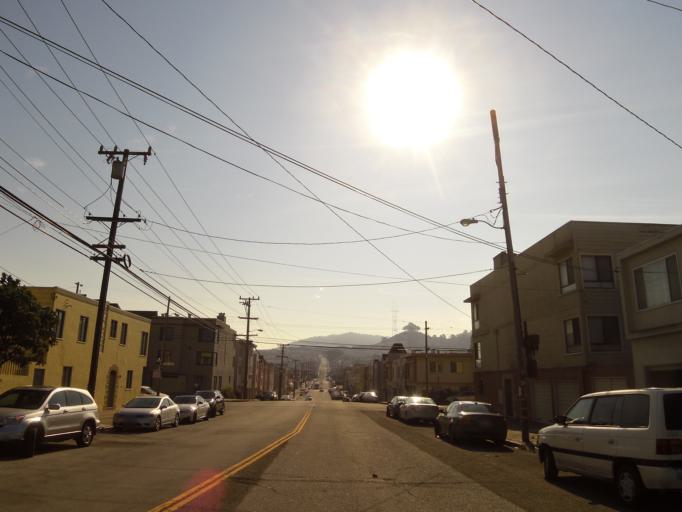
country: US
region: California
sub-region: San Mateo County
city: Daly City
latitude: 37.7576
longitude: -122.4859
